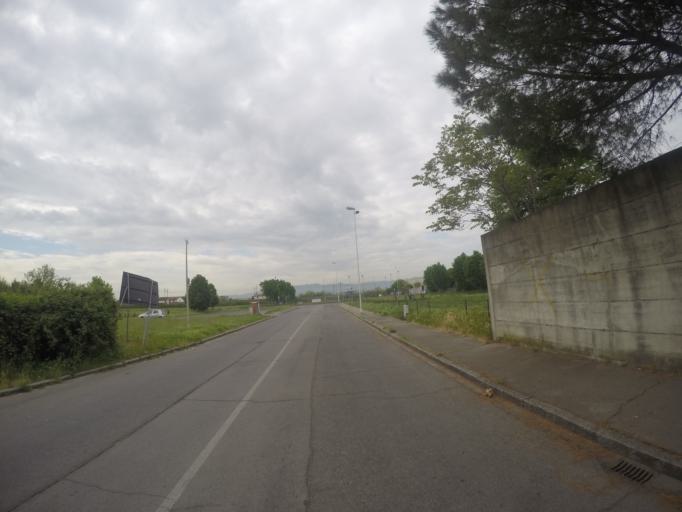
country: IT
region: Tuscany
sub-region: Provincia di Prato
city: Fornacelle
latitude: 43.8966
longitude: 11.0548
